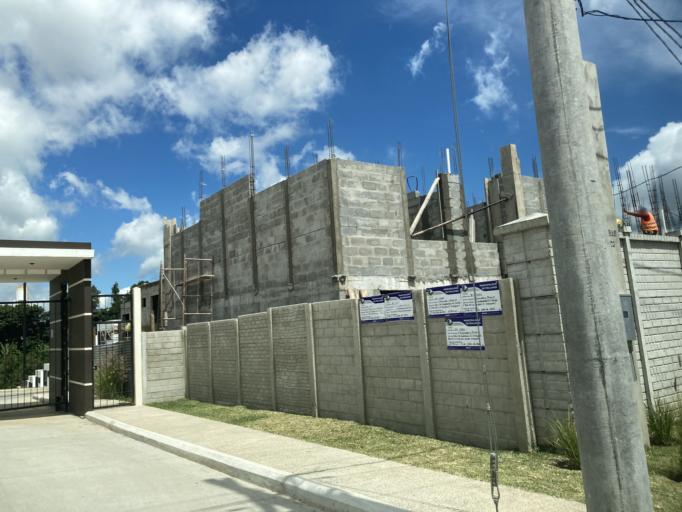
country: GT
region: Guatemala
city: San Jose Pinula
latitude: 14.5376
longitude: -90.4357
